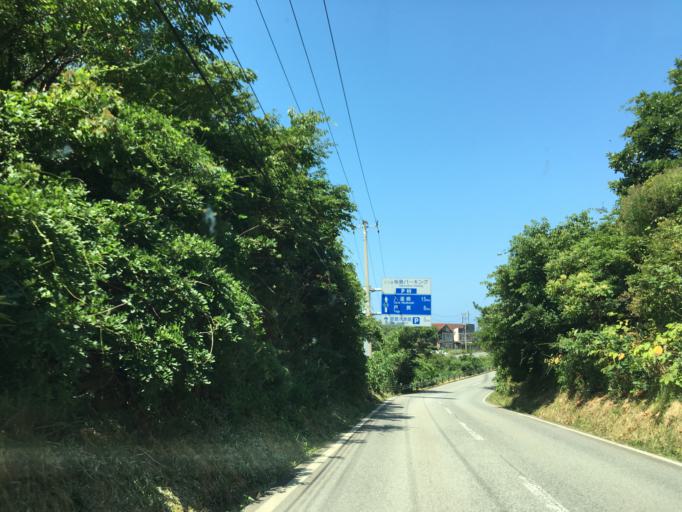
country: JP
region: Akita
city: Tenno
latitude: 39.9096
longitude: 139.7240
